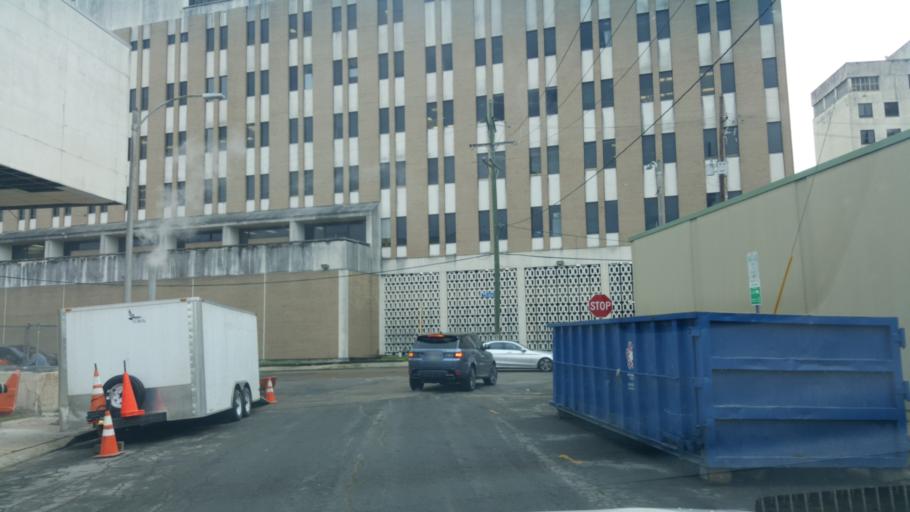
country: US
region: Louisiana
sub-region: Orleans Parish
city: New Orleans
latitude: 29.9540
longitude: -90.0811
